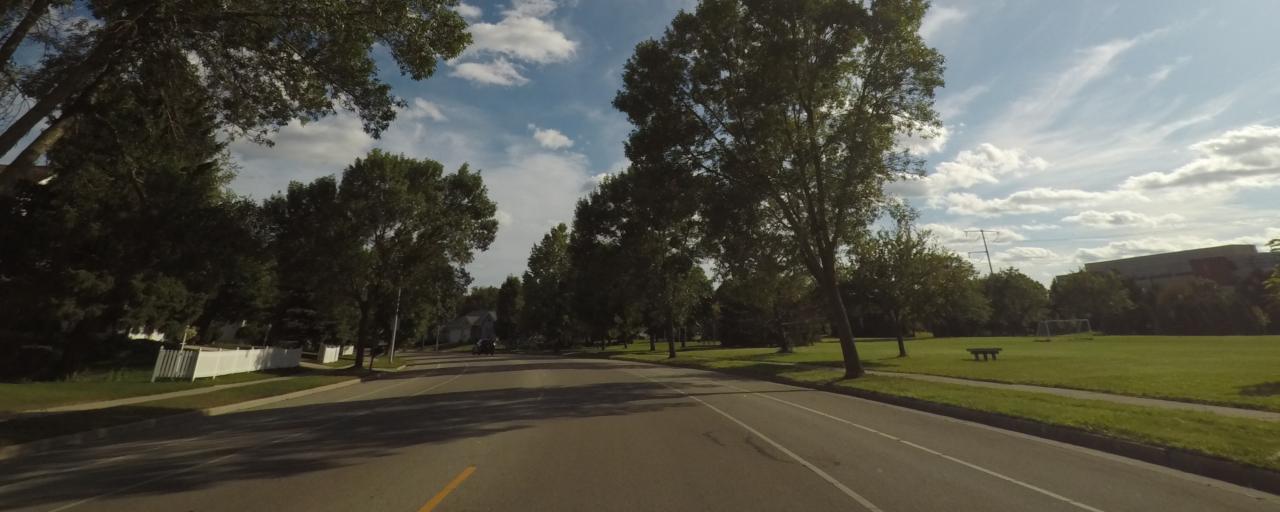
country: US
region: Wisconsin
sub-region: Dane County
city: Middleton
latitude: 43.0716
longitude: -89.5205
